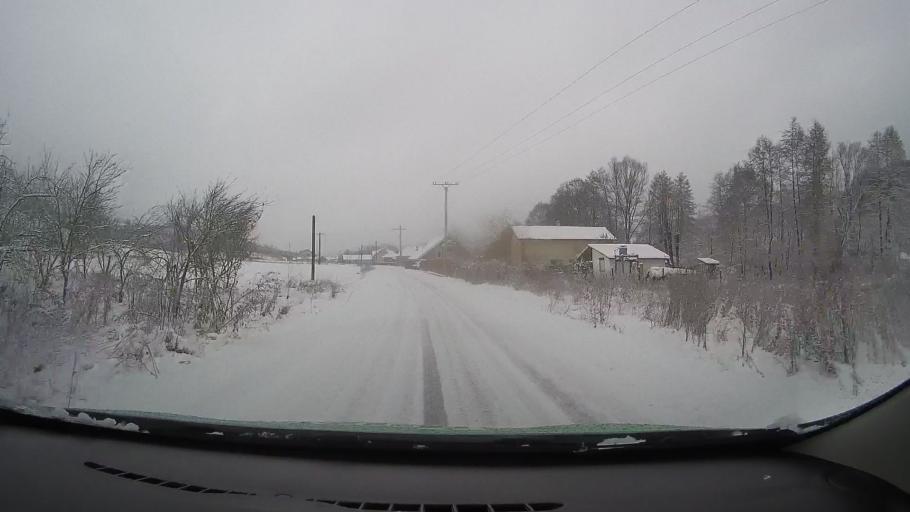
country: RO
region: Hunedoara
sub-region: Comuna Carjiti
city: Carjiti
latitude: 45.8311
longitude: 22.8425
